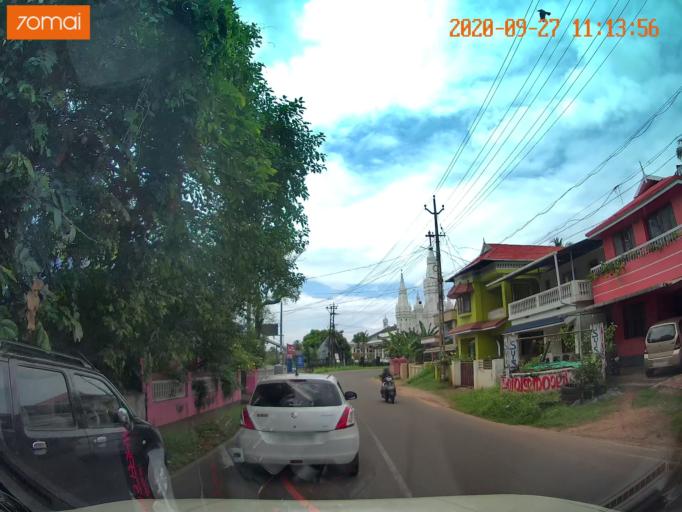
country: IN
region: Kerala
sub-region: Thrissur District
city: Thanniyam
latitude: 10.4343
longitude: 76.2074
